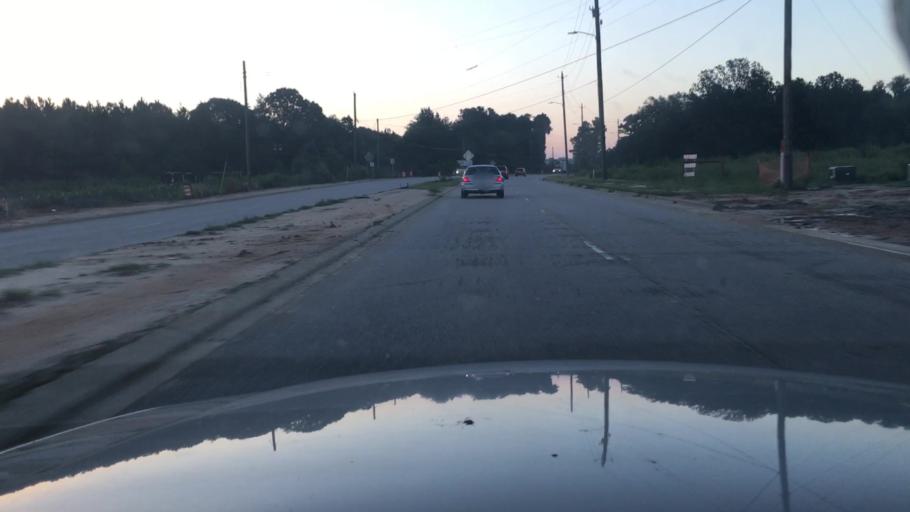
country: US
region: North Carolina
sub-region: Cumberland County
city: Fort Bragg
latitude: 35.0637
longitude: -79.0216
